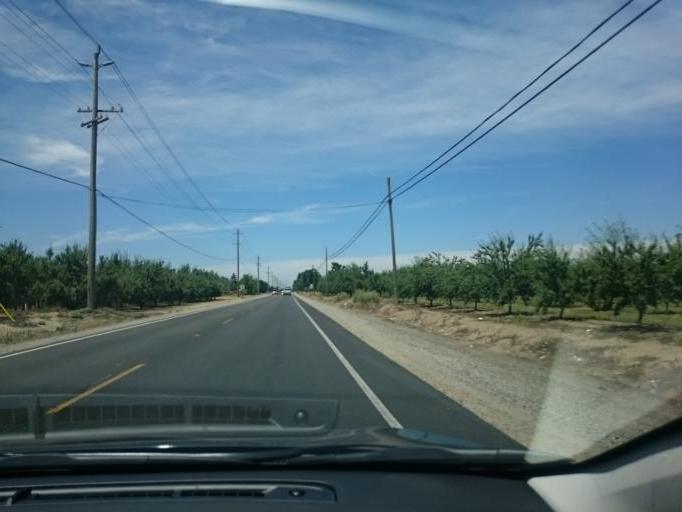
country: US
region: California
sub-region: Stanislaus County
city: Waterford
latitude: 37.6383
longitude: -120.7833
